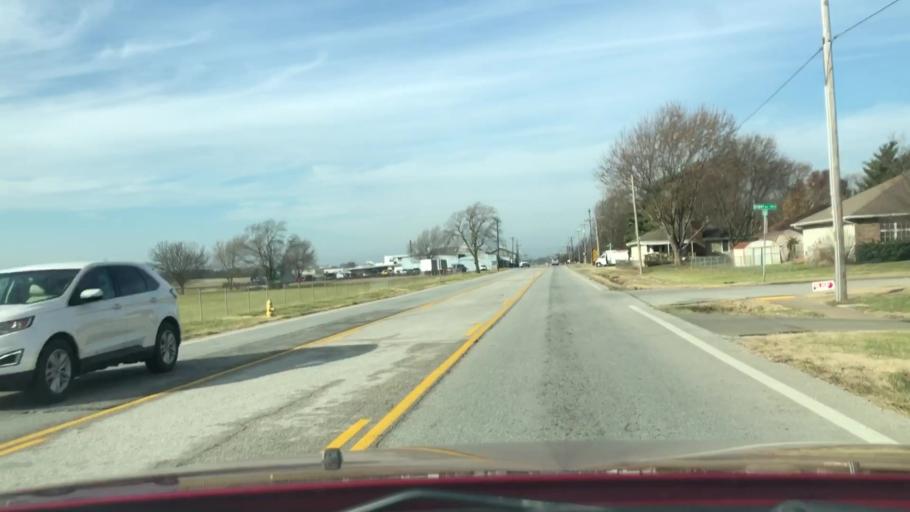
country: US
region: Missouri
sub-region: Greene County
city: Springfield
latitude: 37.2250
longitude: -93.2449
